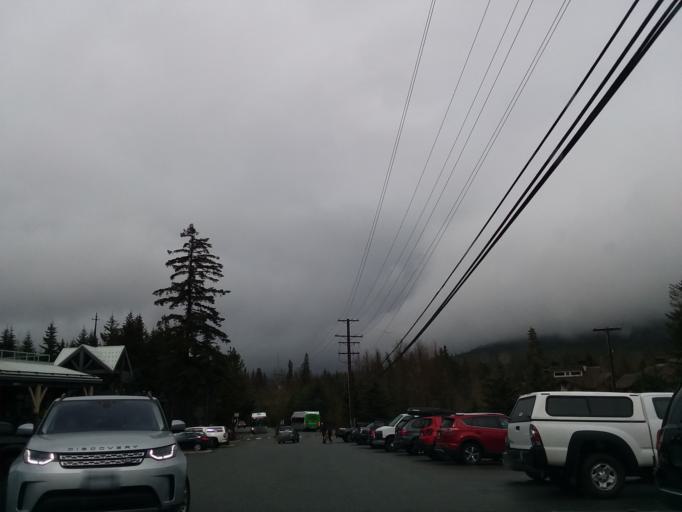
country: CA
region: British Columbia
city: Whistler
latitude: 50.1274
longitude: -122.9554
